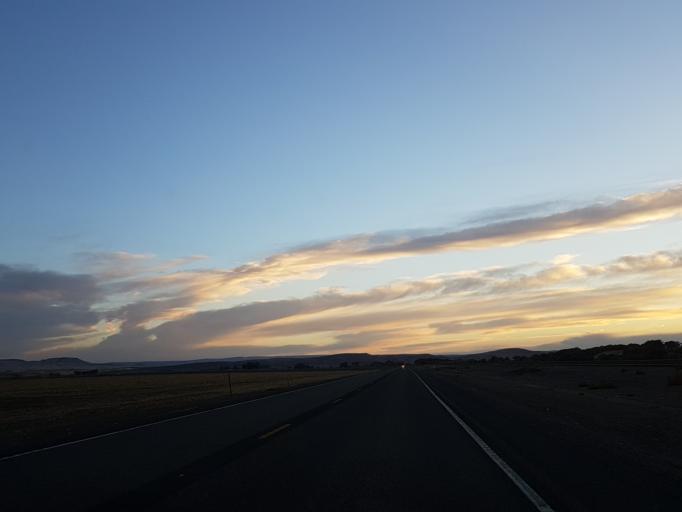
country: US
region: Oregon
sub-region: Malheur County
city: Vale
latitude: 43.9539
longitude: -117.2895
